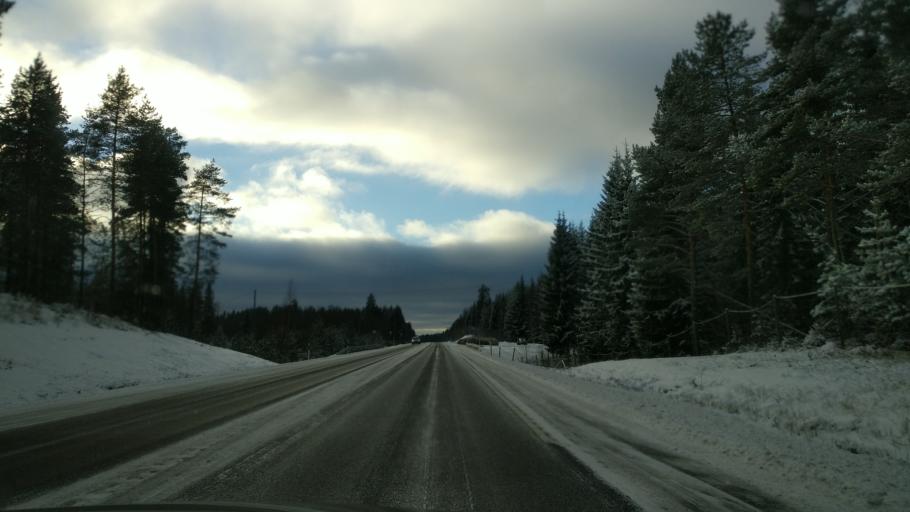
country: FI
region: Paijanne Tavastia
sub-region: Lahti
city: Heinola
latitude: 61.3473
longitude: 26.2076
